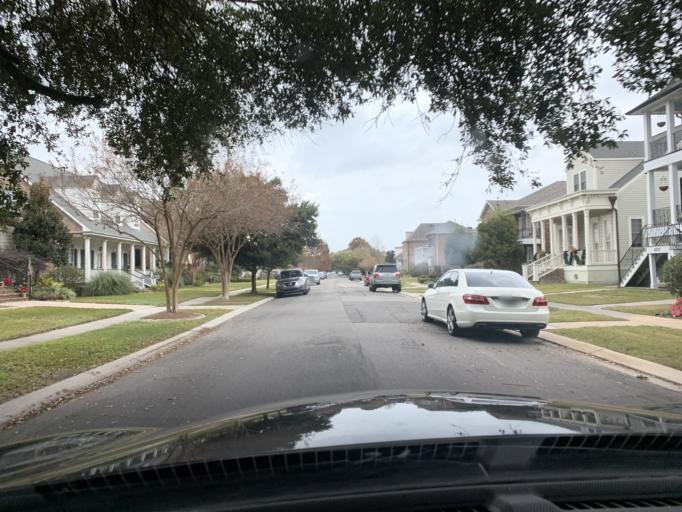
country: US
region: Louisiana
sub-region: Jefferson Parish
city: Metairie
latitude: 30.0046
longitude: -90.1015
